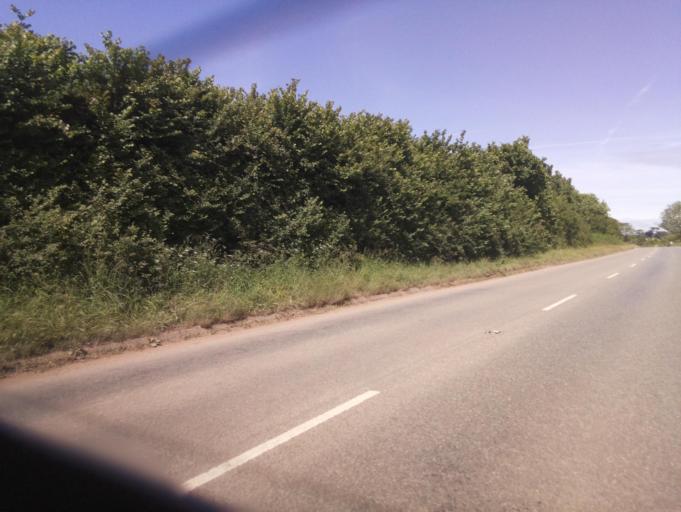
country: GB
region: England
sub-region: Devon
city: Budleigh Salterton
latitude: 50.6420
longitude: -3.3170
